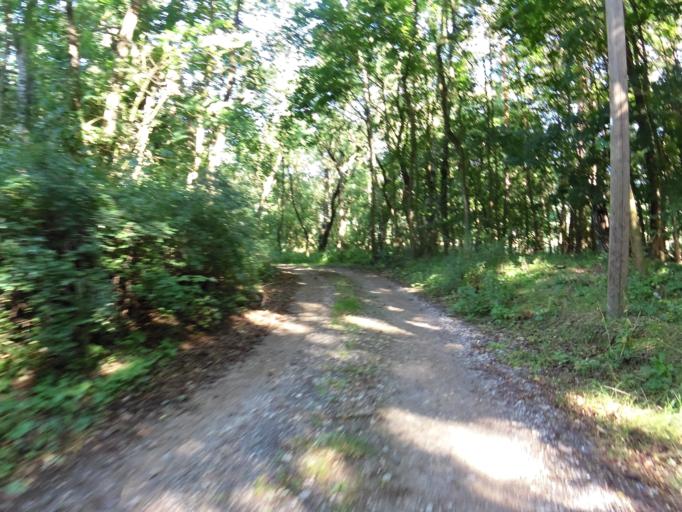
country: DE
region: Saxony-Anhalt
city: Coswig
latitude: 51.8826
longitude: 12.5022
